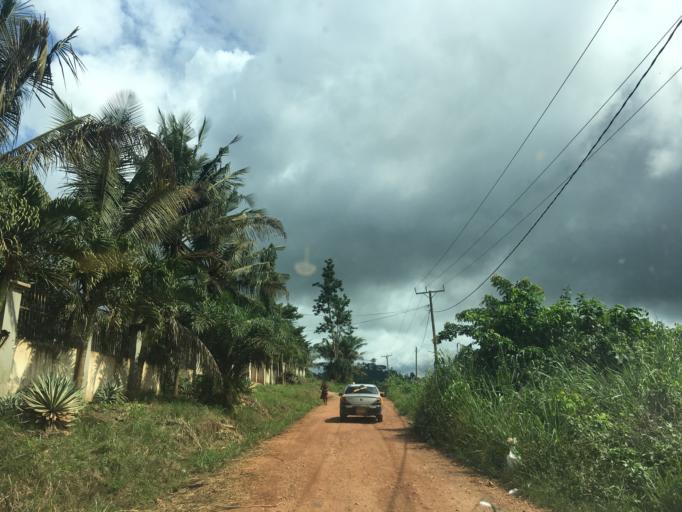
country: GH
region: Western
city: Wassa-Akropong
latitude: 5.7911
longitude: -2.4291
